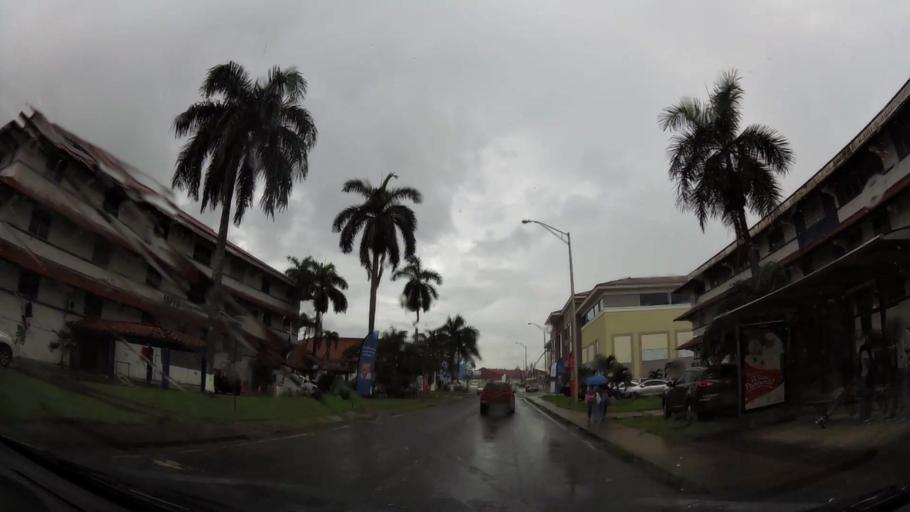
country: PA
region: Panama
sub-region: Distrito de Panama
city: Ancon
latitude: 8.9721
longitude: -79.5617
